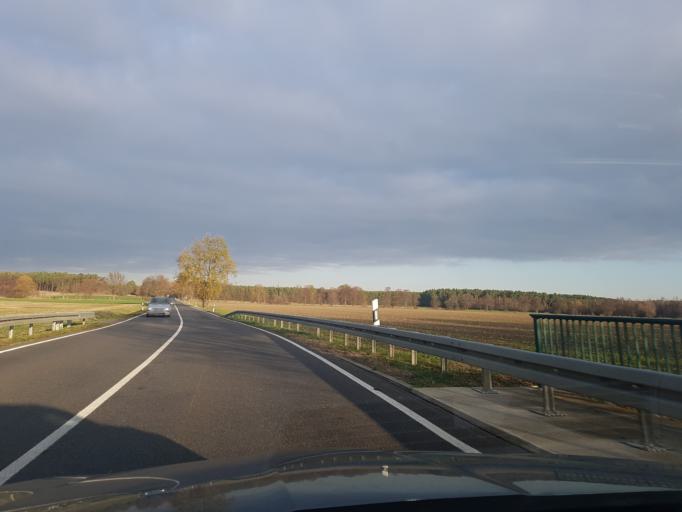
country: DE
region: Brandenburg
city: Kasel-Golzig
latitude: 51.9041
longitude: 13.6744
